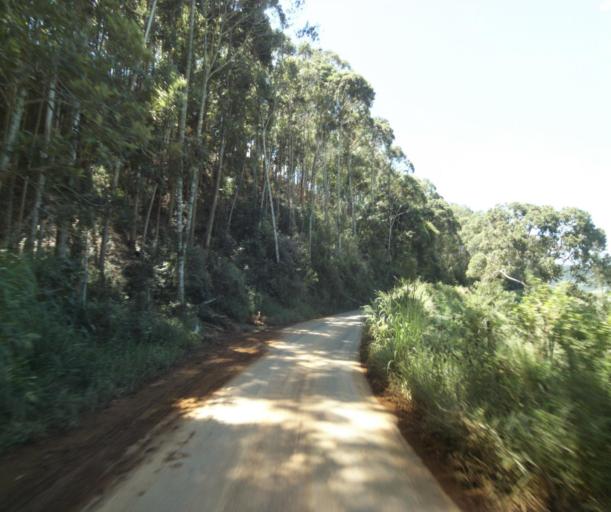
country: BR
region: Minas Gerais
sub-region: Espera Feliz
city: Espera Feliz
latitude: -20.6238
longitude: -41.8335
